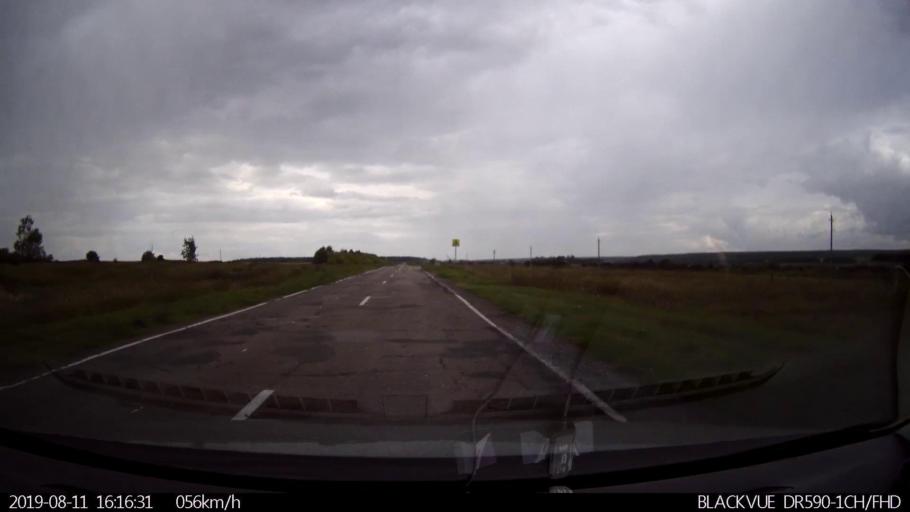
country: RU
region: Ulyanovsk
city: Mayna
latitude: 54.0417
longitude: 47.6210
